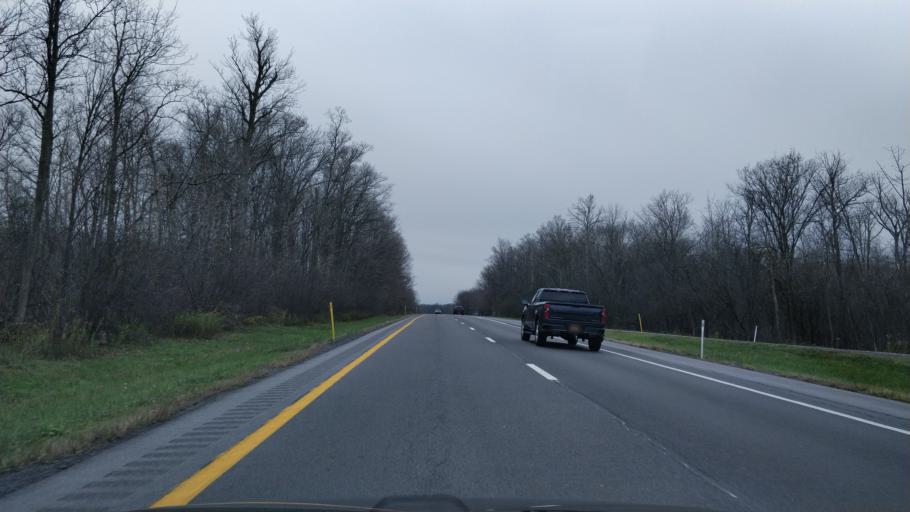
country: US
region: New York
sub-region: Jefferson County
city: Adams
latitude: 43.7367
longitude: -76.0748
